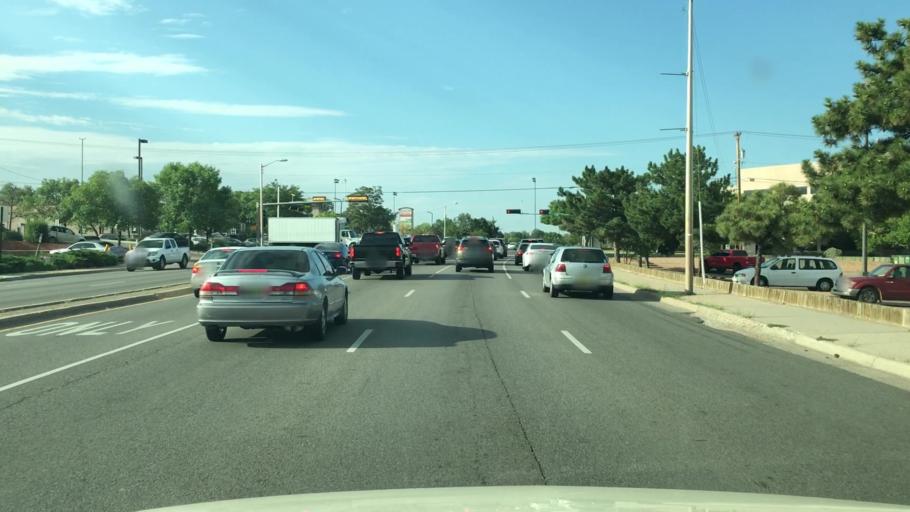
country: US
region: New Mexico
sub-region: Santa Fe County
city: Santa Fe
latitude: 35.6750
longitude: -105.9536
